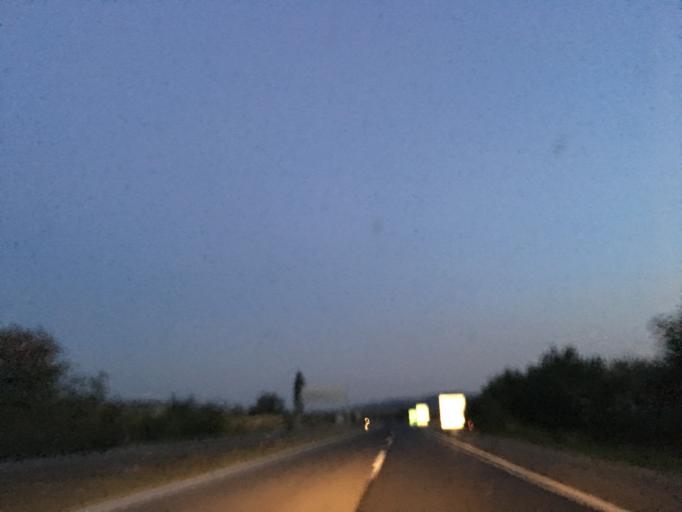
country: MK
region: Petrovec
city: Petrovec
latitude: 41.9299
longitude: 21.6296
